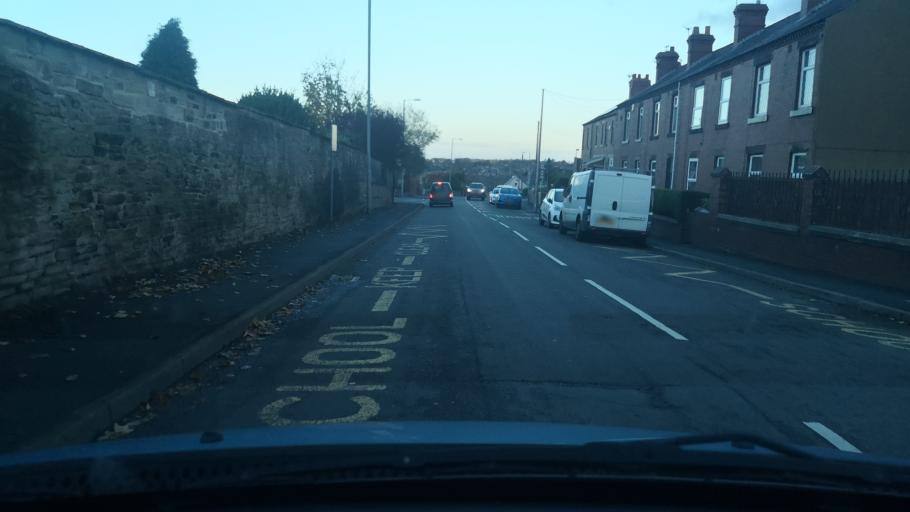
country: GB
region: England
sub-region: City and Borough of Wakefield
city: Horbury
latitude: 53.6484
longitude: -1.5756
